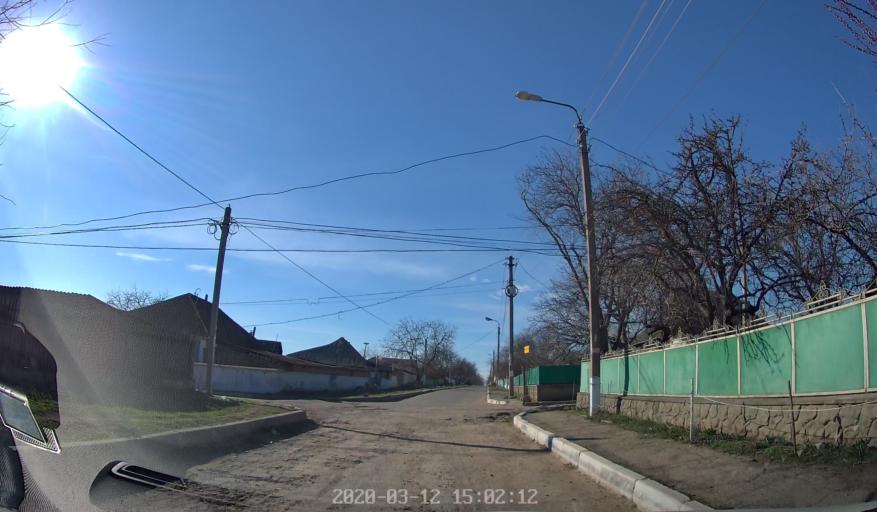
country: MD
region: Telenesti
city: Cocieri
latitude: 47.2223
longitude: 29.0273
